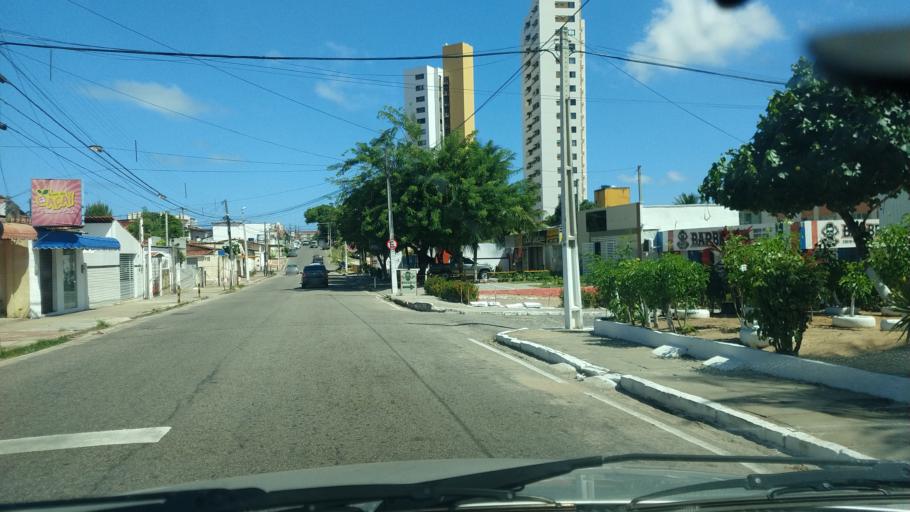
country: BR
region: Rio Grande do Norte
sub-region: Natal
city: Natal
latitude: -5.8581
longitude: -35.2101
